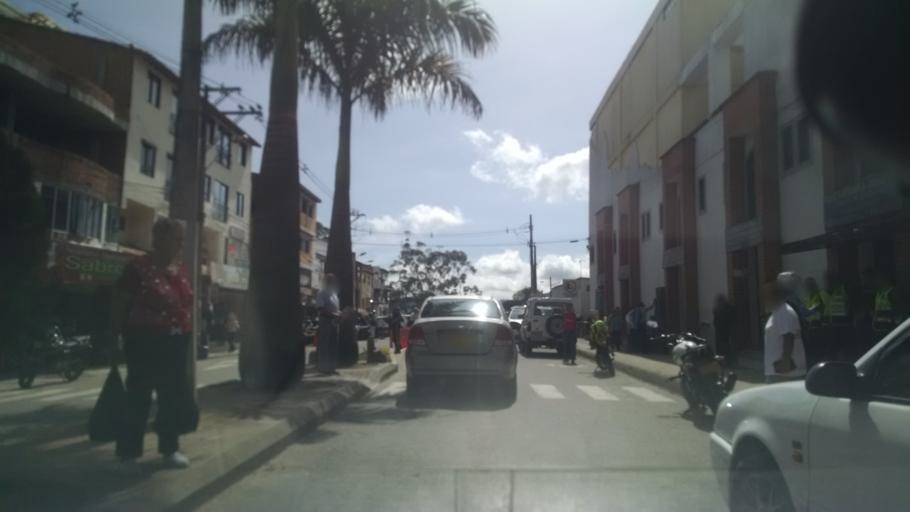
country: CO
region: Antioquia
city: Guatape
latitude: 6.2175
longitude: -75.2429
